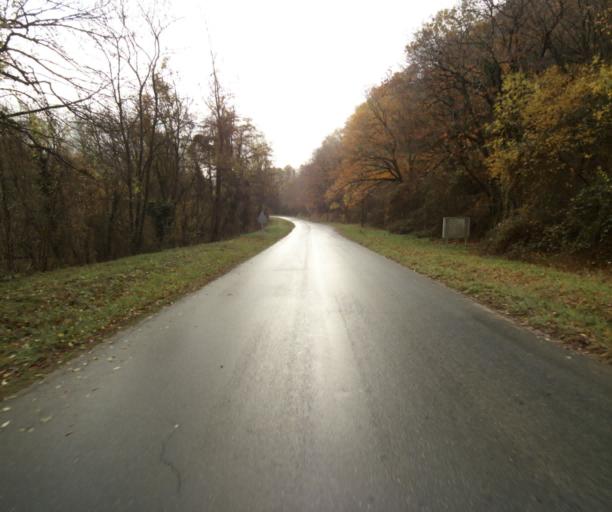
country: FR
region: Limousin
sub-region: Departement de la Correze
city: Cornil
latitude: 45.1891
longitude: 1.6518
